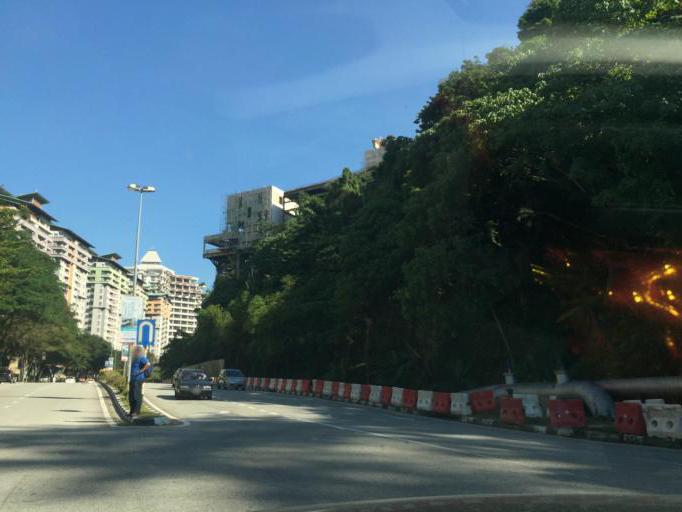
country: MY
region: Selangor
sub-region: Petaling
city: Petaling Jaya
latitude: 3.1672
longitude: 101.6067
